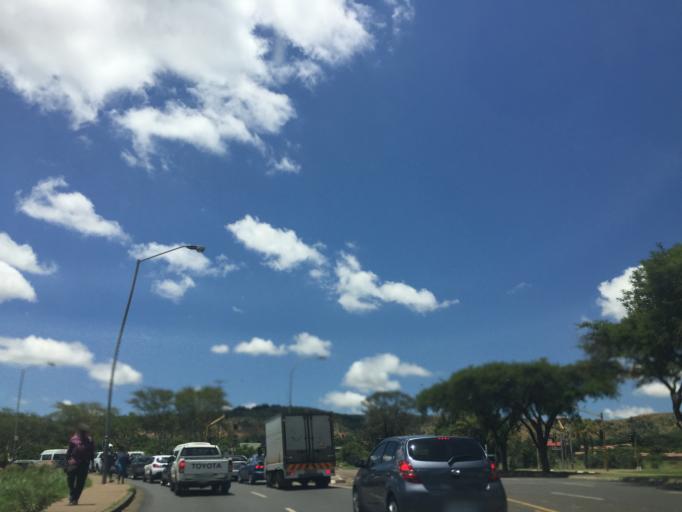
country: ZA
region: Gauteng
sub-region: City of Tshwane Metropolitan Municipality
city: Pretoria
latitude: -25.6739
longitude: 28.1088
